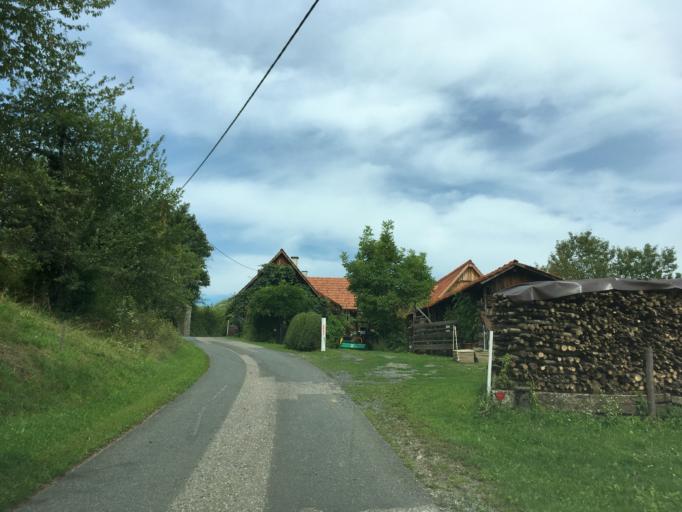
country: AT
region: Styria
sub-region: Politischer Bezirk Deutschlandsberg
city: Wettmannstatten
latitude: 46.7957
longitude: 15.3998
